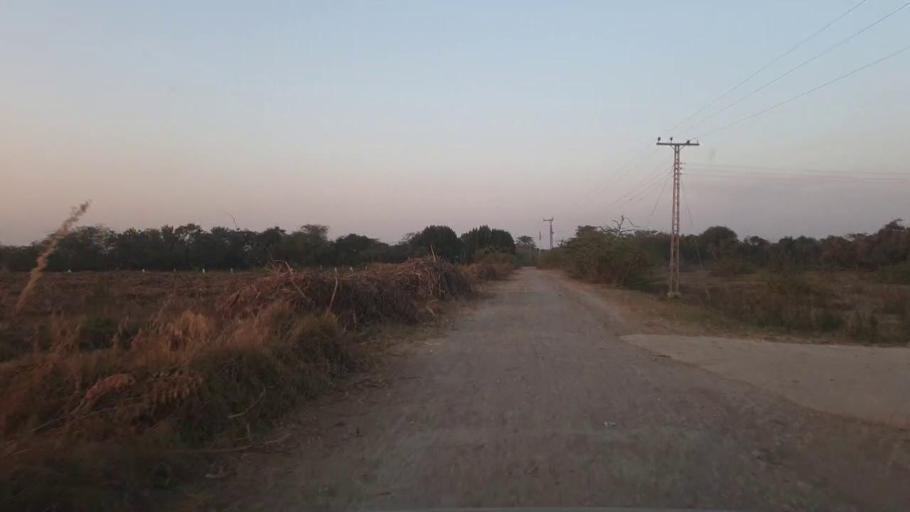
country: PK
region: Sindh
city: Chambar
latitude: 25.3098
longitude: 68.9075
